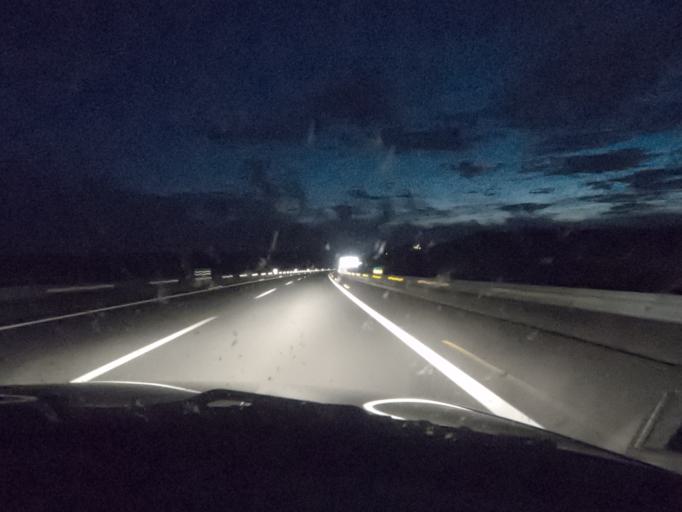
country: ES
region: Extremadura
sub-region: Provincia de Caceres
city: Coria
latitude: 39.9850
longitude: -6.4860
